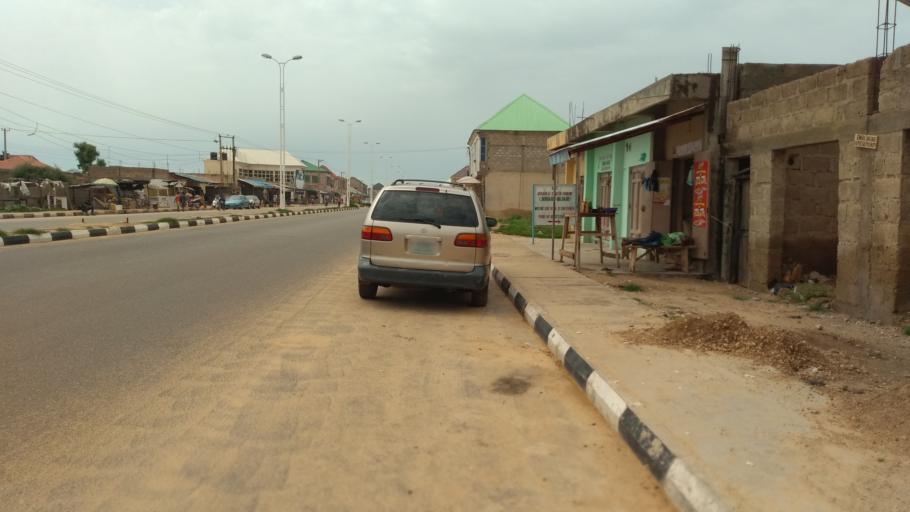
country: NG
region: Katsina
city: Katsina
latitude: 12.9769
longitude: 7.6418
